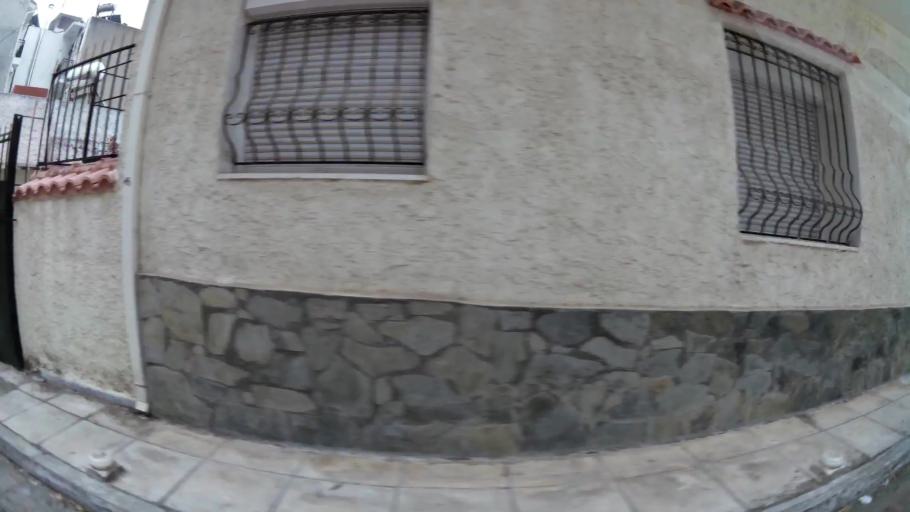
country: GR
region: Attica
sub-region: Nomarchia Athinas
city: Ilion
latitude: 38.0203
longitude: 23.7057
